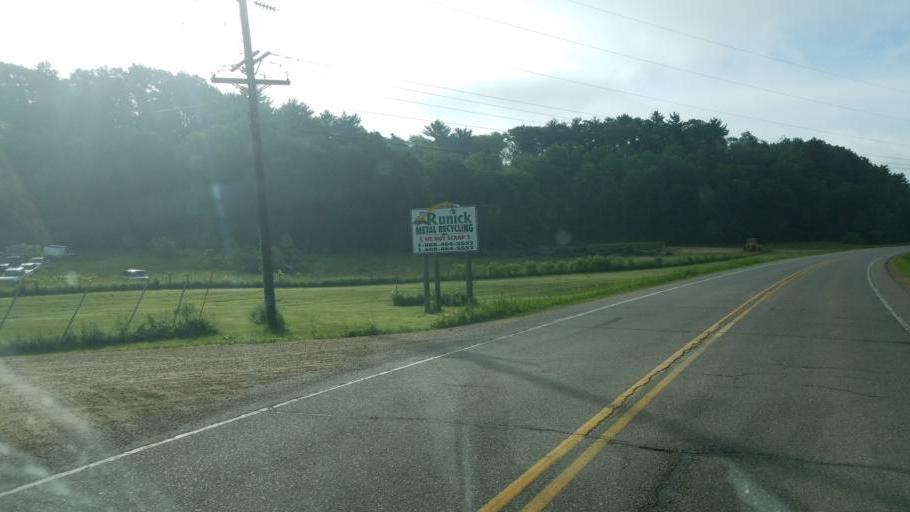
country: US
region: Wisconsin
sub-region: Juneau County
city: Elroy
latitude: 43.6776
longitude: -90.2552
